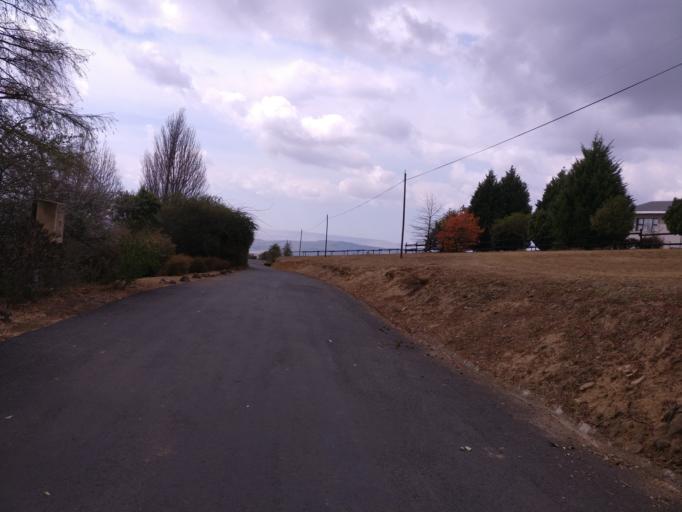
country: ZA
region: KwaZulu-Natal
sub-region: uThukela District Municipality
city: Bergville
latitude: -29.0146
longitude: 29.4231
